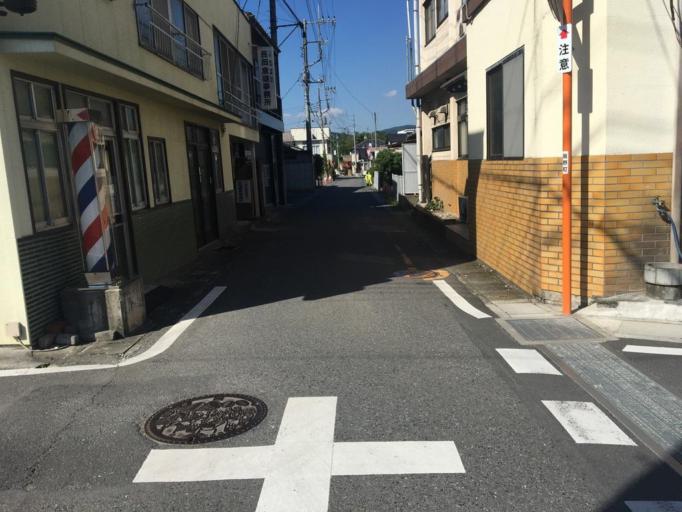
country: JP
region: Saitama
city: Chichibu
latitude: 36.0696
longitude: 139.0946
